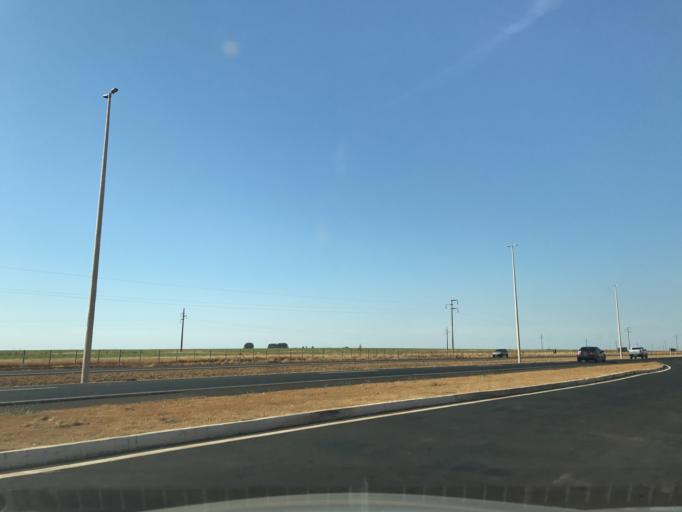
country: BR
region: Goias
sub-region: Morrinhos
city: Morrinhos
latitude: -17.8442
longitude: -49.2190
